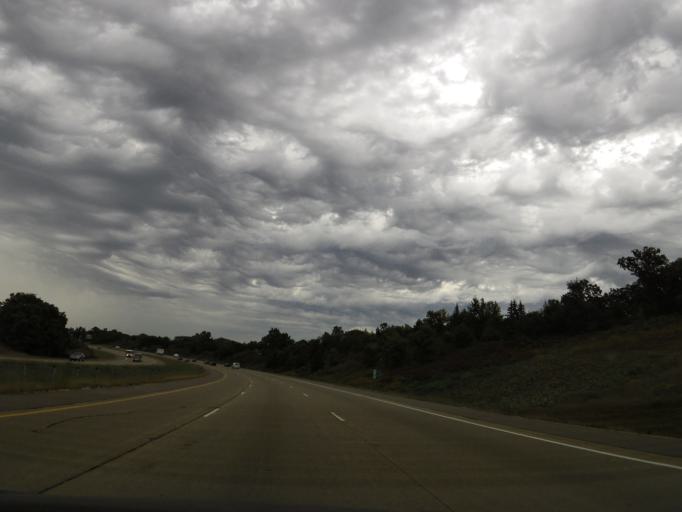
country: US
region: Minnesota
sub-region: Dakota County
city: Eagan
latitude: 44.8152
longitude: -93.1740
